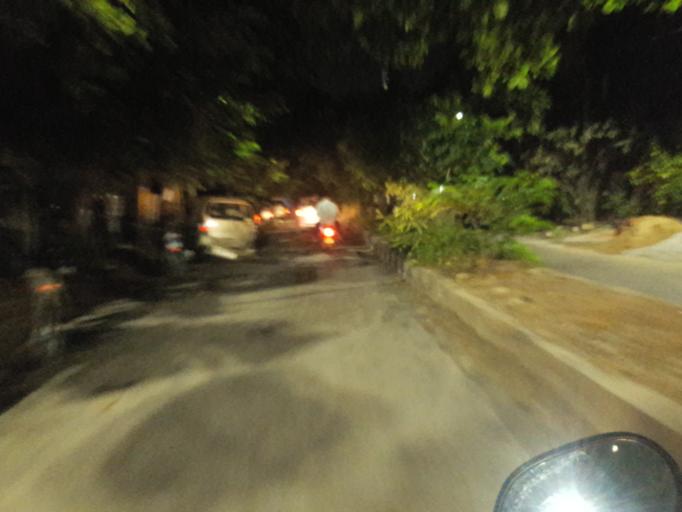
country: IN
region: Telangana
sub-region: Rangareddi
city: Kukatpalli
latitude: 17.4826
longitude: 78.3910
